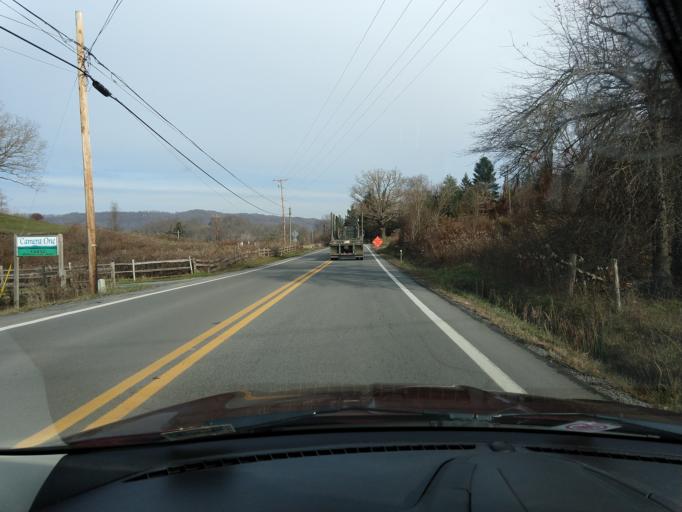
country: US
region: West Virginia
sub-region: Greenbrier County
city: Rainelle
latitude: 37.9444
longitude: -80.6525
